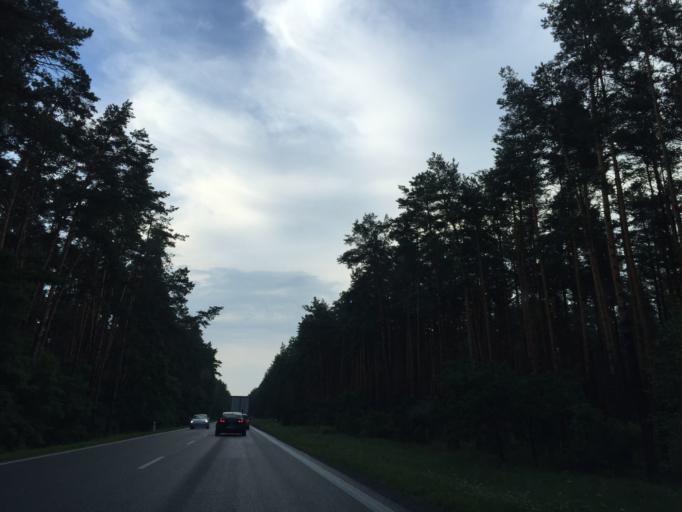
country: PL
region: Masovian Voivodeship
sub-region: Powiat ostrowski
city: Brok
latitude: 52.7140
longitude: 21.8486
